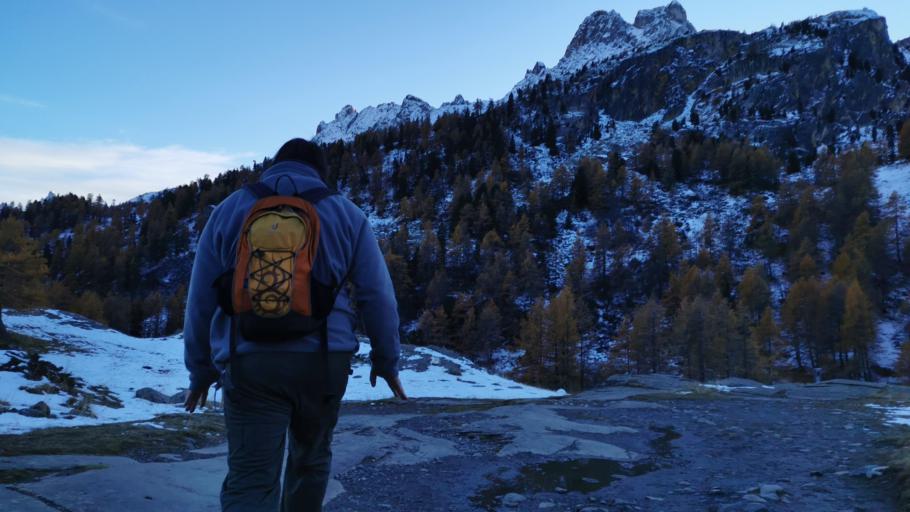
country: FR
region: Provence-Alpes-Cote d'Azur
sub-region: Departement des Hautes-Alpes
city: Le Monetier-les-Bains
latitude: 45.0602
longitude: 6.5249
